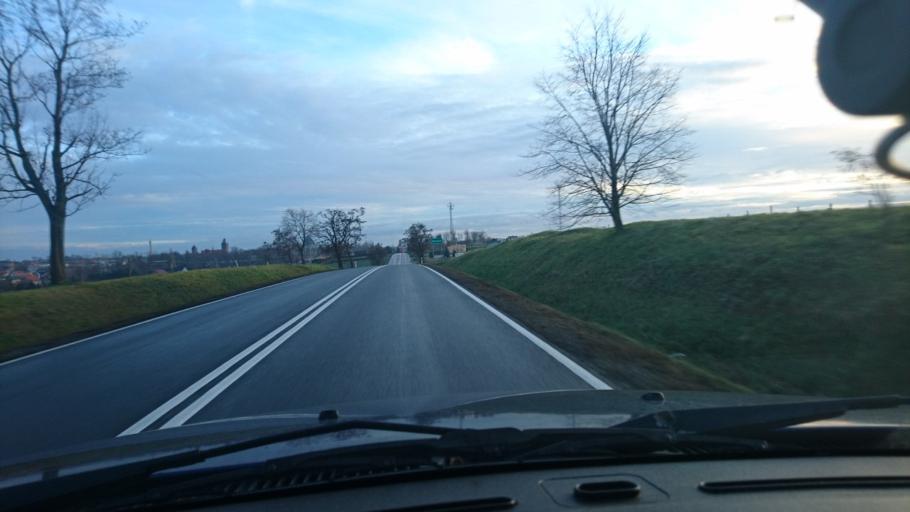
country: PL
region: Opole Voivodeship
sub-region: Powiat kluczborski
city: Byczyna
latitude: 51.1223
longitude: 18.2054
